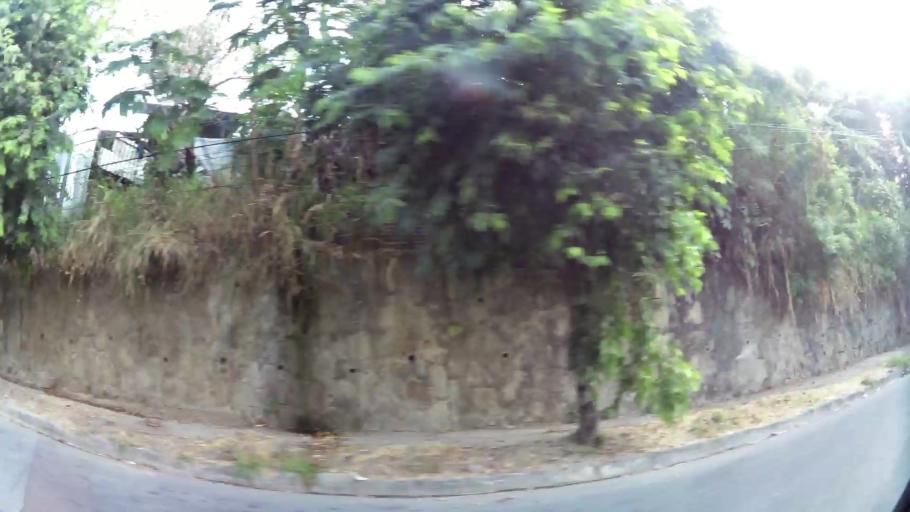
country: SV
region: San Salvador
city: San Salvador
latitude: 13.6773
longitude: -89.2029
